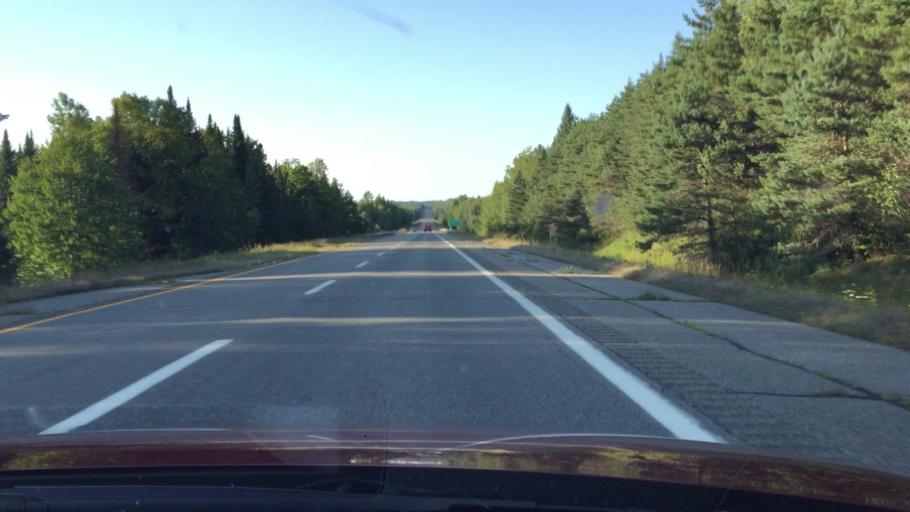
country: US
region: Maine
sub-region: Penobscot County
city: Patten
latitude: 45.8092
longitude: -68.4282
